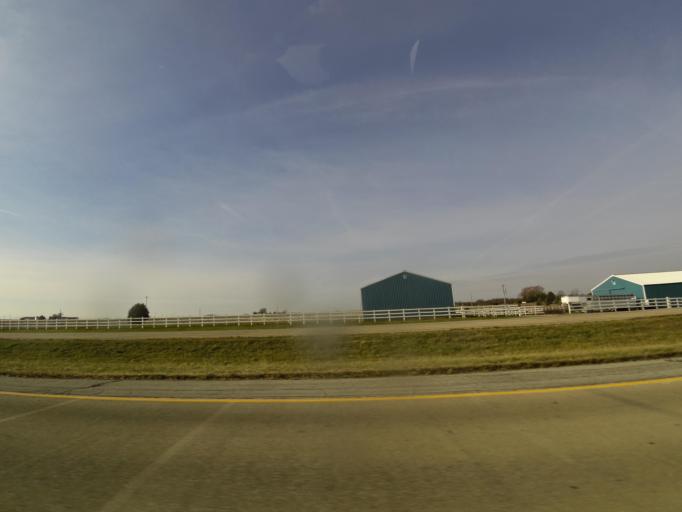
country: US
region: Illinois
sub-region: Macon County
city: Maroa
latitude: 40.0826
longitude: -88.9656
